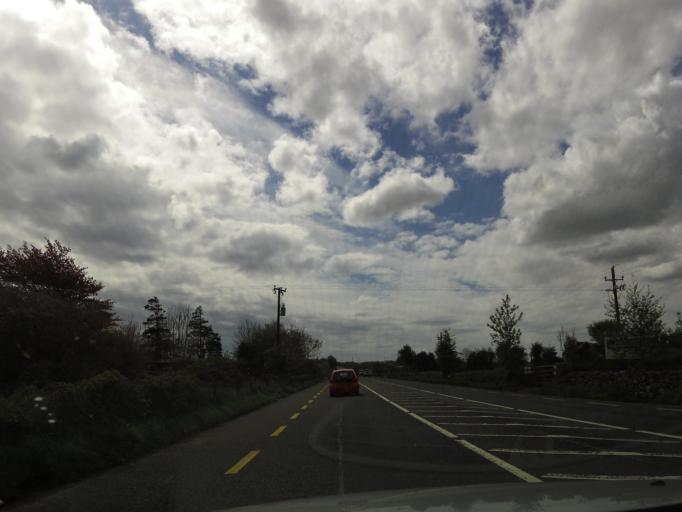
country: IE
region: Connaught
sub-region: County Galway
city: Claregalway
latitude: 53.3264
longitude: -8.9680
